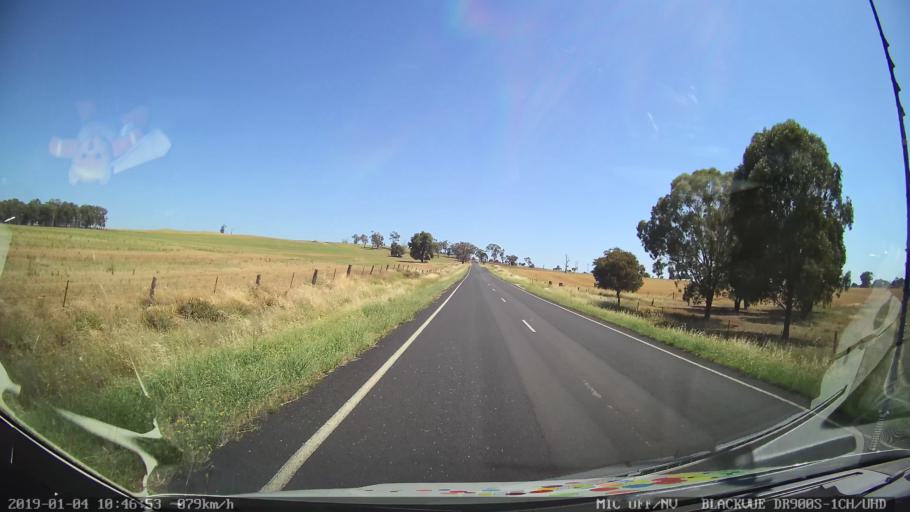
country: AU
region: New South Wales
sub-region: Cabonne
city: Molong
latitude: -33.2759
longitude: 148.7209
